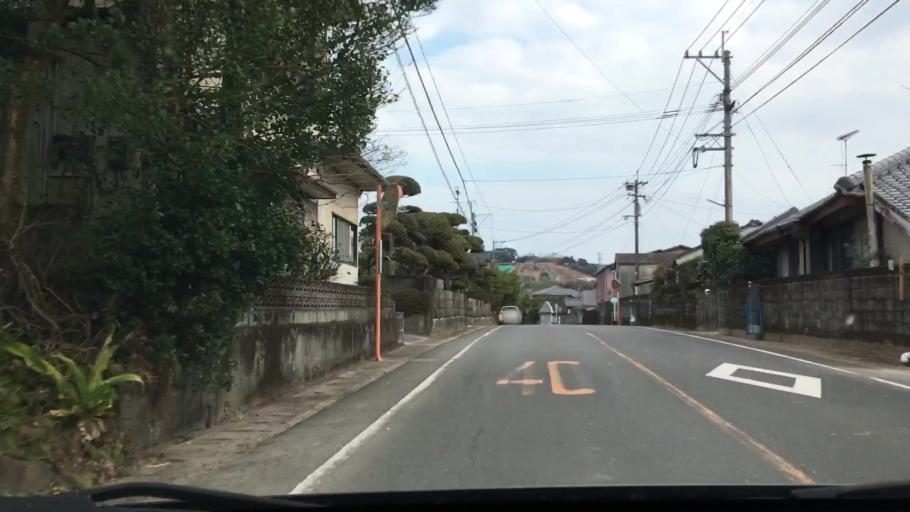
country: JP
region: Miyazaki
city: Kushima
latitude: 31.4678
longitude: 131.2104
